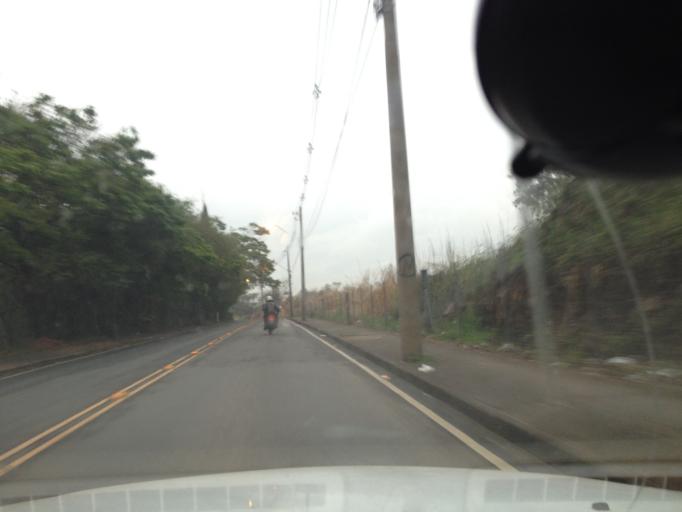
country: BR
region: Sao Paulo
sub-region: Salto
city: Salto
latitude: -23.2064
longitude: -47.2746
